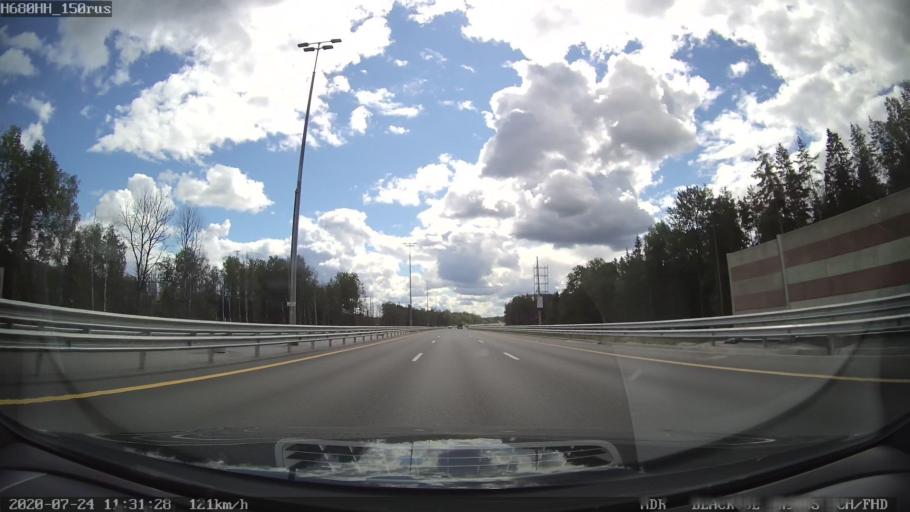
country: RU
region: Leningrad
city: Krasnyy Bor
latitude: 59.6566
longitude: 30.6379
